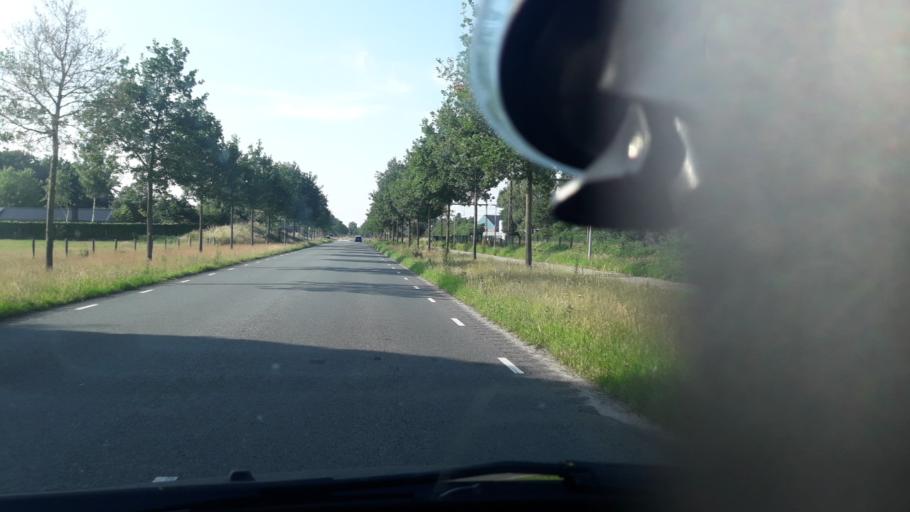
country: NL
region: Gelderland
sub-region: Gemeente Ermelo
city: Ermelo
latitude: 52.3152
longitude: 5.6150
